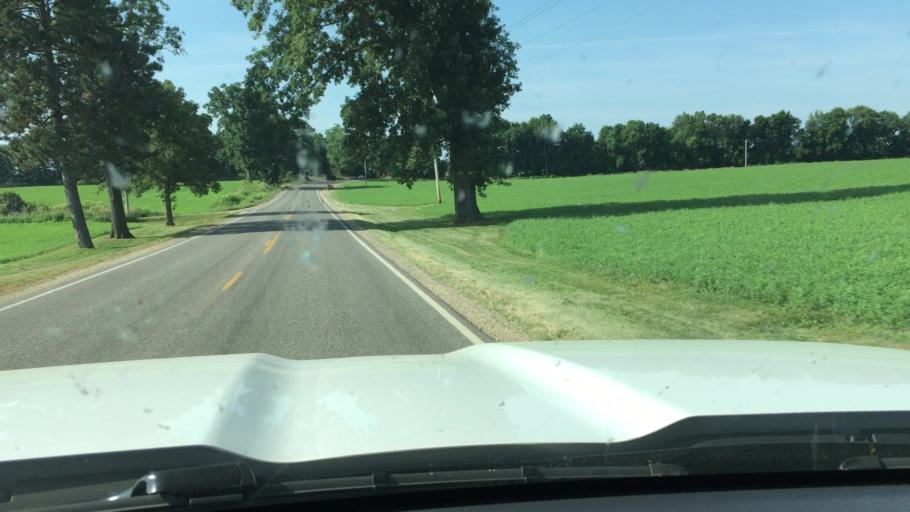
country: US
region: Michigan
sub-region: Kalamazoo County
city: South Gull Lake
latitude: 42.4235
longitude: -85.4547
